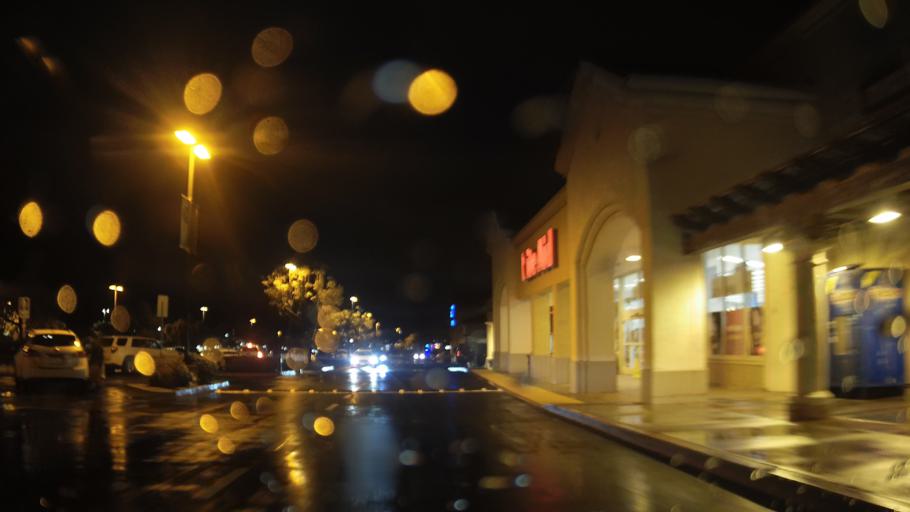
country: US
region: California
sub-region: San Diego County
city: Rancho San Diego
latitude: 32.7458
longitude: -116.9301
